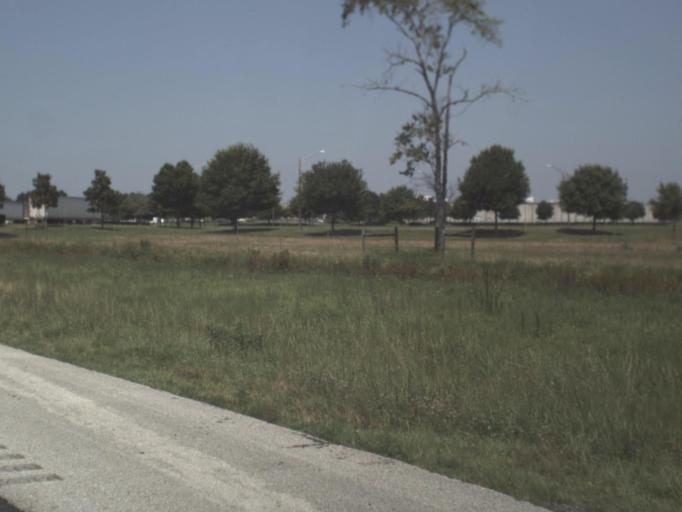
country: US
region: Florida
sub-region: Duval County
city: Baldwin
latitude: 30.2978
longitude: -81.9376
